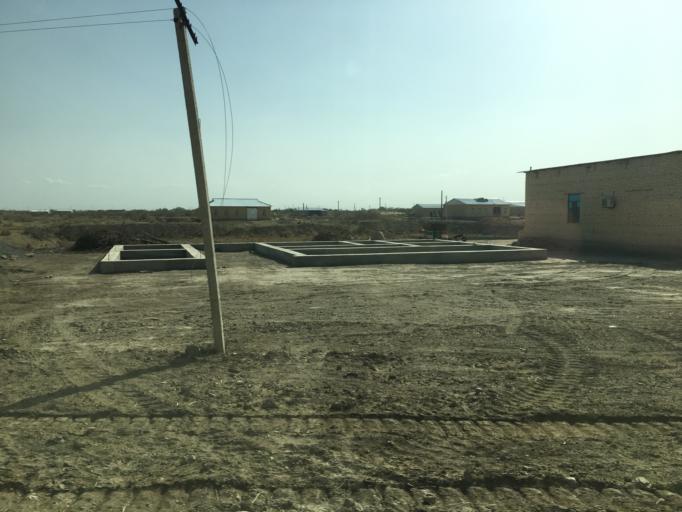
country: TM
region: Lebap
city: Farap
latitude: 39.3084
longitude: 63.3829
